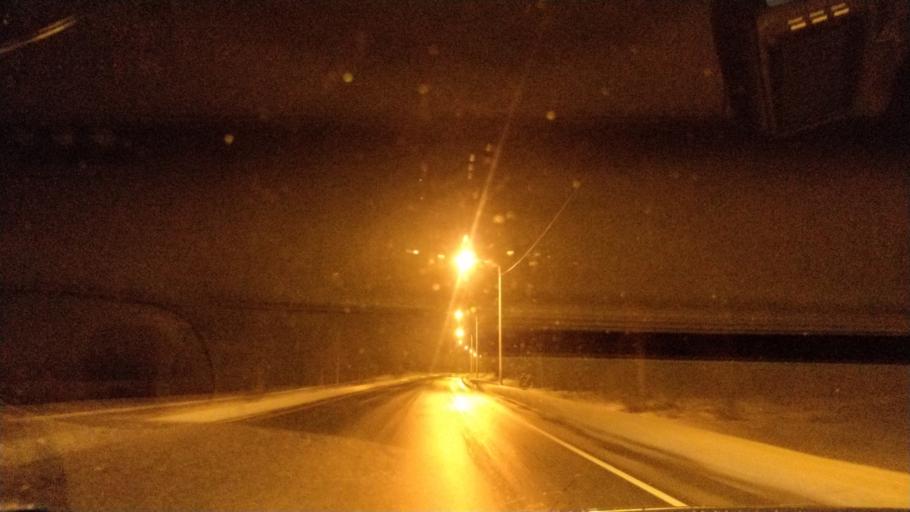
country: FI
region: Lapland
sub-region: Kemi-Tornio
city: Tervola
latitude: 66.1373
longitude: 24.9332
